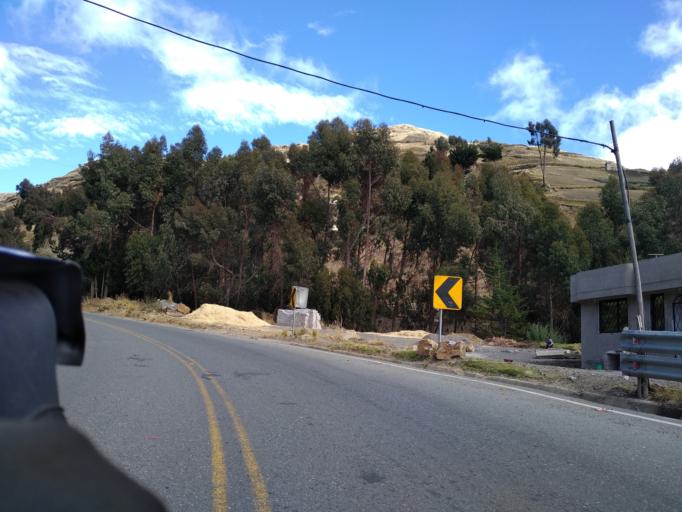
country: EC
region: Cotopaxi
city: Pujili
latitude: -0.9613
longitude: -78.9110
